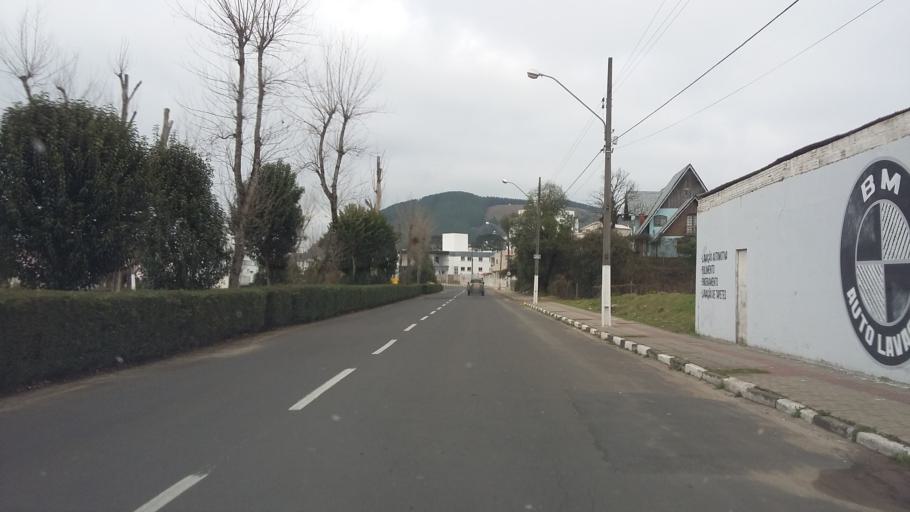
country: BR
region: Santa Catarina
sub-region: Lages
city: Lages
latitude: -27.8207
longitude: -50.3218
